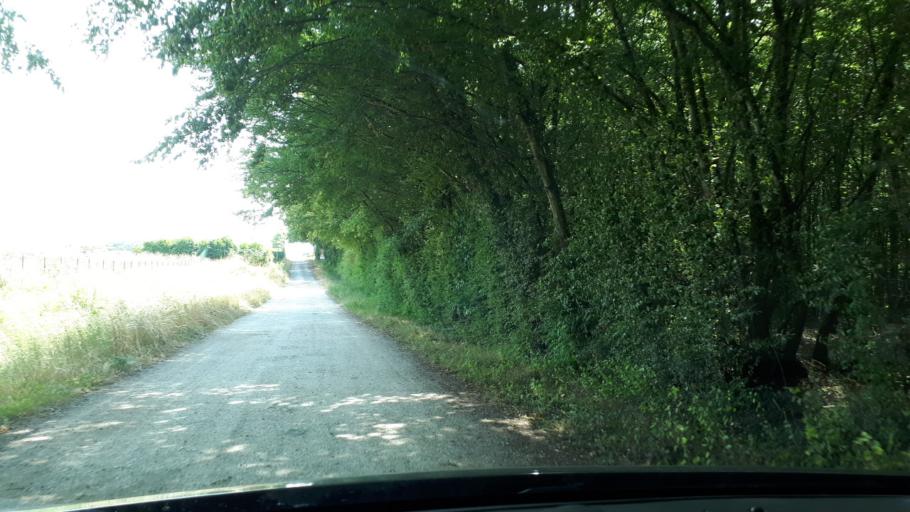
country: FR
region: Centre
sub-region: Departement du Loir-et-Cher
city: Saint-Ouen
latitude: 47.8271
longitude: 1.0536
